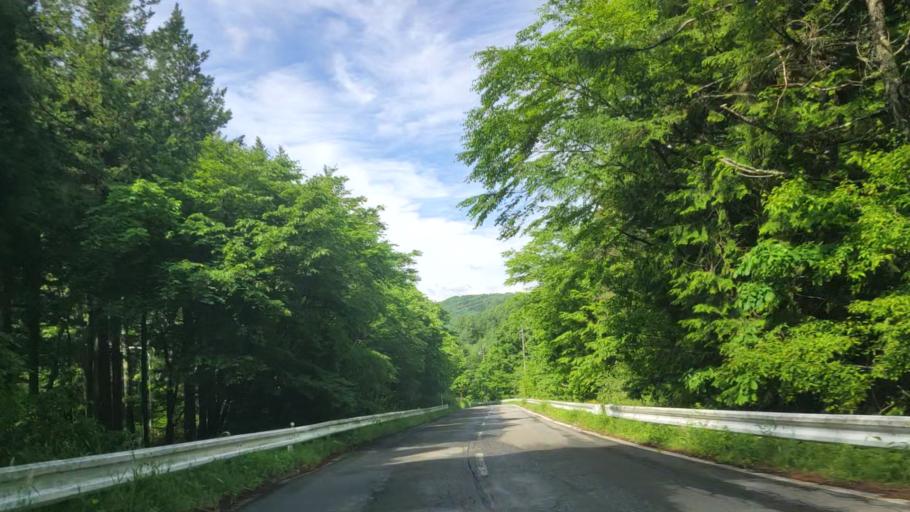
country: JP
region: Nagano
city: Suwa
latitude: 36.0845
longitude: 138.1431
